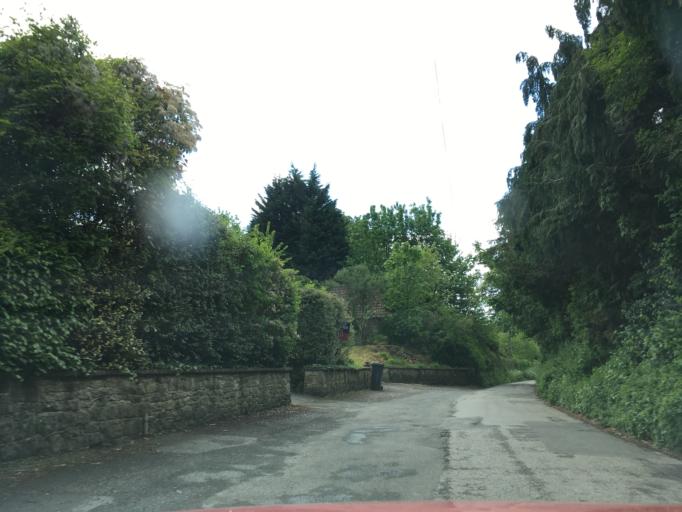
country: GB
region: England
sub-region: Gloucestershire
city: Dursley
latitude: 51.6871
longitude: -2.3931
